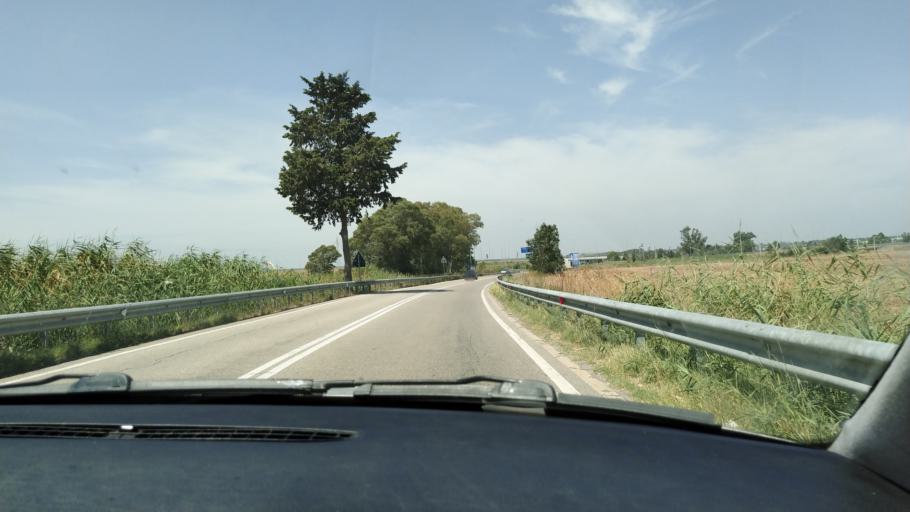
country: IT
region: Apulia
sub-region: Provincia di Taranto
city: Marina di Ginosa
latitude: 40.3757
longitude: 16.7942
